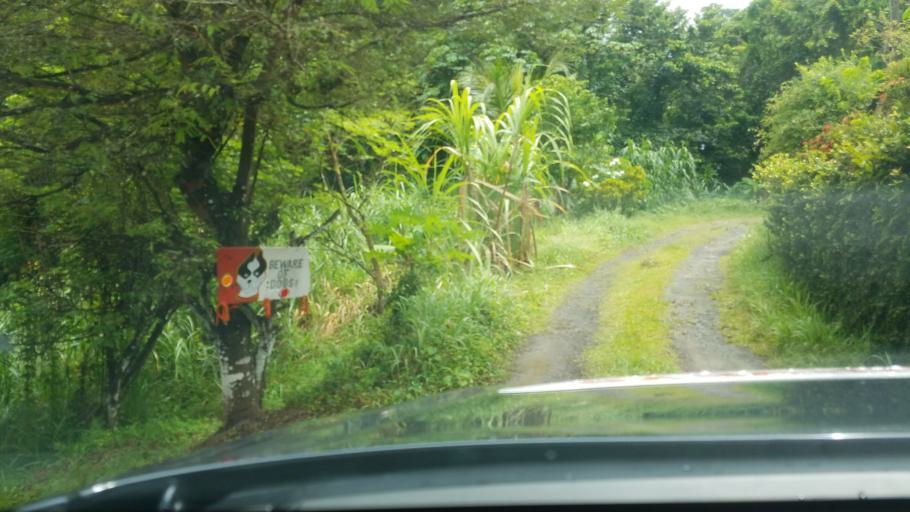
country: LC
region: Castries Quarter
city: Castries
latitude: 13.9953
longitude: -61.0010
